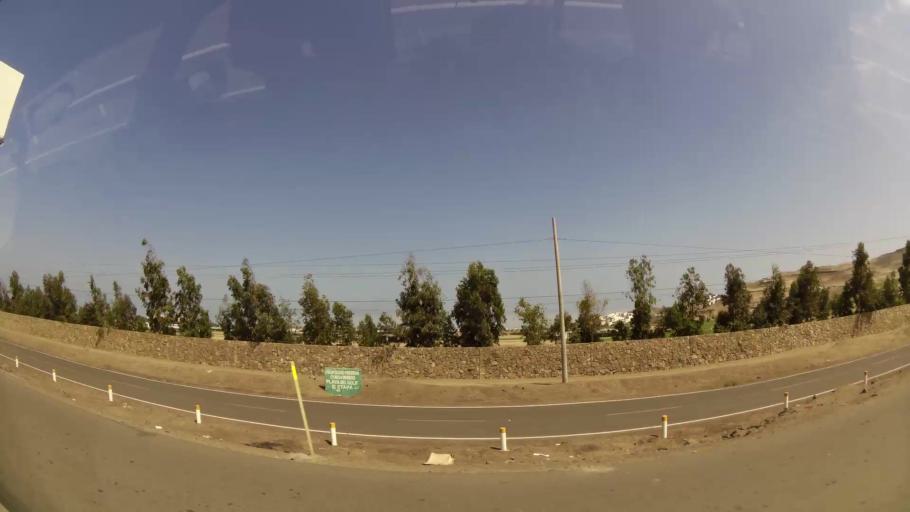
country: PE
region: Lima
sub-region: Provincia de Canete
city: Asia
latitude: -12.7478
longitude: -76.6104
